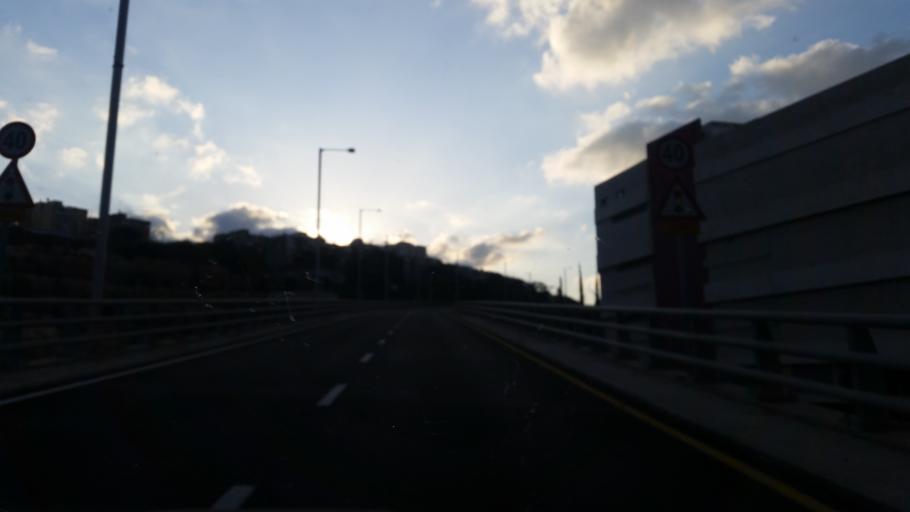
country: IL
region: Haifa
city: Haifa
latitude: 32.7904
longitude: 35.0078
